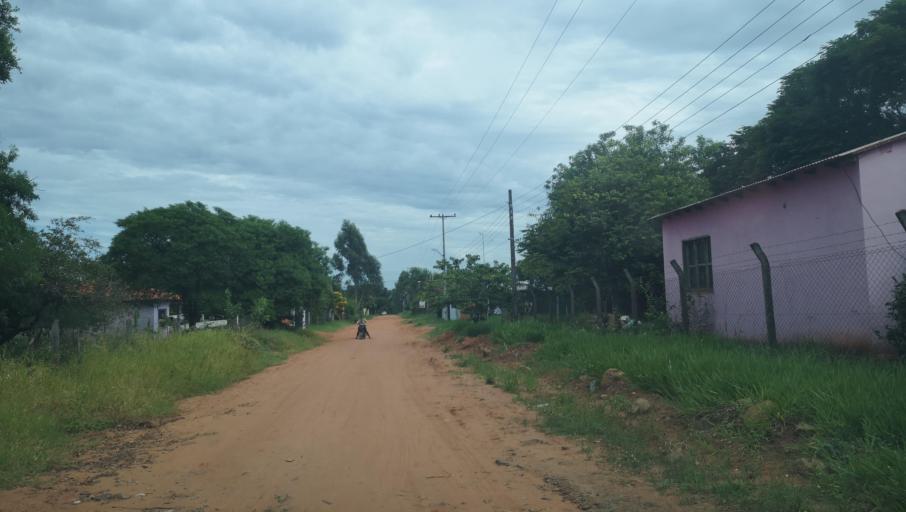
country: PY
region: San Pedro
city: Capiibary
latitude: -24.7256
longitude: -56.0192
